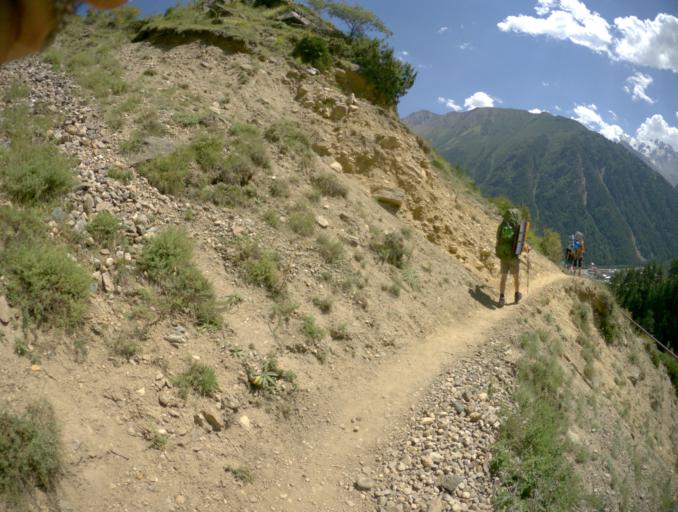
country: RU
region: Kabardino-Balkariya
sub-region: El'brusskiy Rayon
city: El'brus
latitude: 43.2632
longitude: 42.6382
